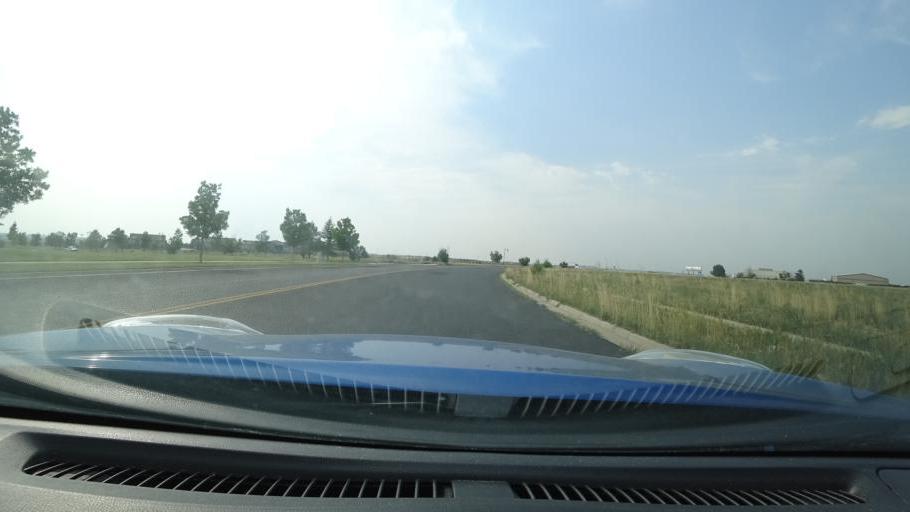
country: US
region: Colorado
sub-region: Adams County
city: Aurora
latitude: 39.7237
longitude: -104.7106
